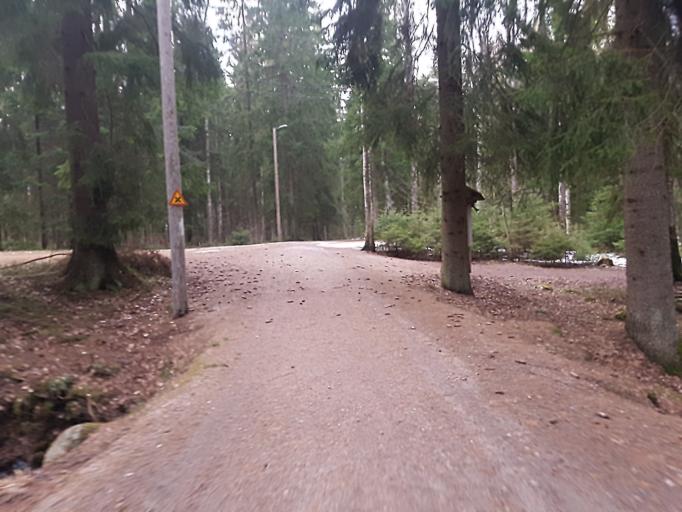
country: FI
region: Uusimaa
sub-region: Helsinki
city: Helsinki
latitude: 60.2652
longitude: 24.9255
